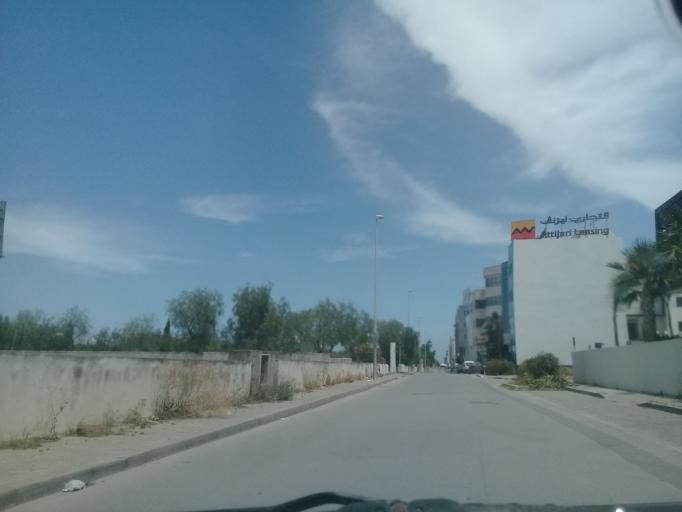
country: TN
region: Ariana
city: Ariana
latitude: 36.8357
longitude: 10.2275
